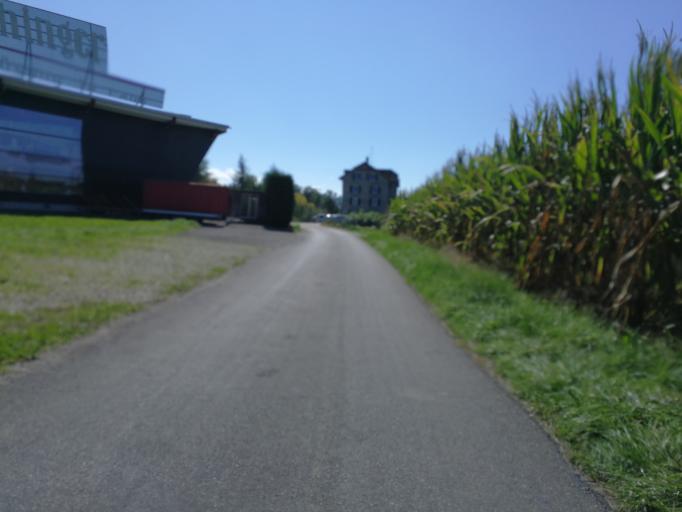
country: CH
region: Zurich
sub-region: Bezirk Hinwil
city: Rueti / Westlicher Dorfteil
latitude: 47.2640
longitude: 8.8340
